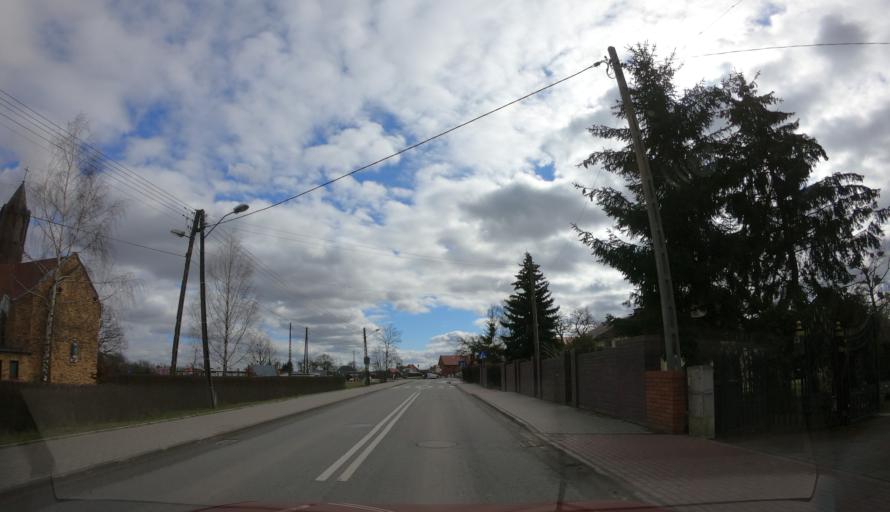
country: PL
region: West Pomeranian Voivodeship
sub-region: Powiat policki
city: Przeclaw
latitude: 53.3752
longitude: 14.4712
